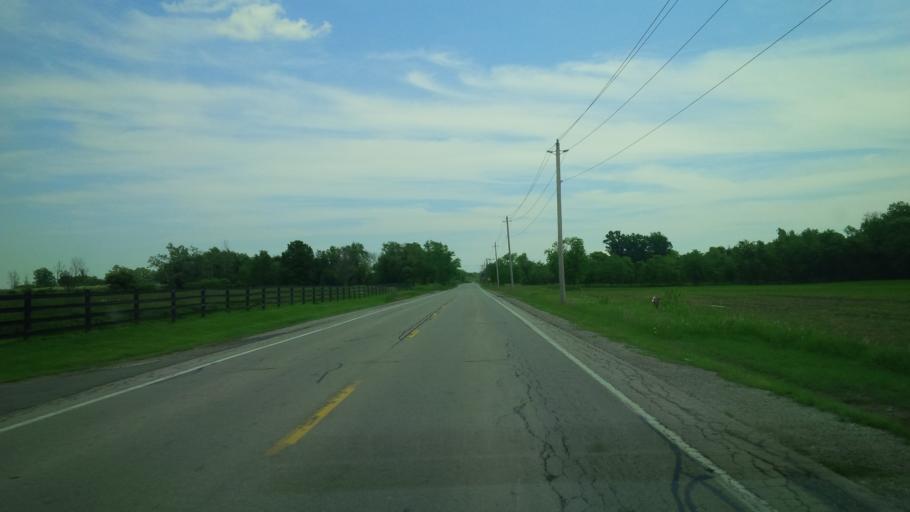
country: CA
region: Ontario
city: Burlington
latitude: 43.4401
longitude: -79.8640
